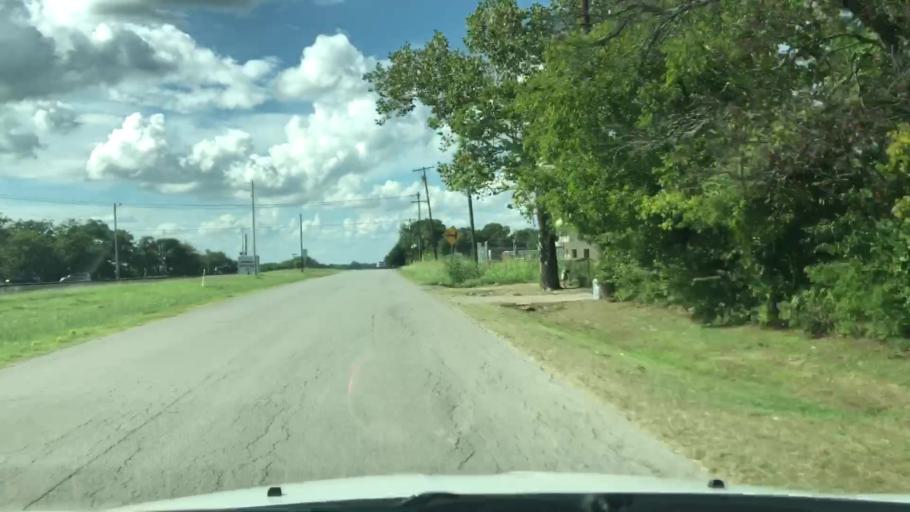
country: US
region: Texas
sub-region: Ellis County
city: Ennis
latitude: 32.3503
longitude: -96.6417
